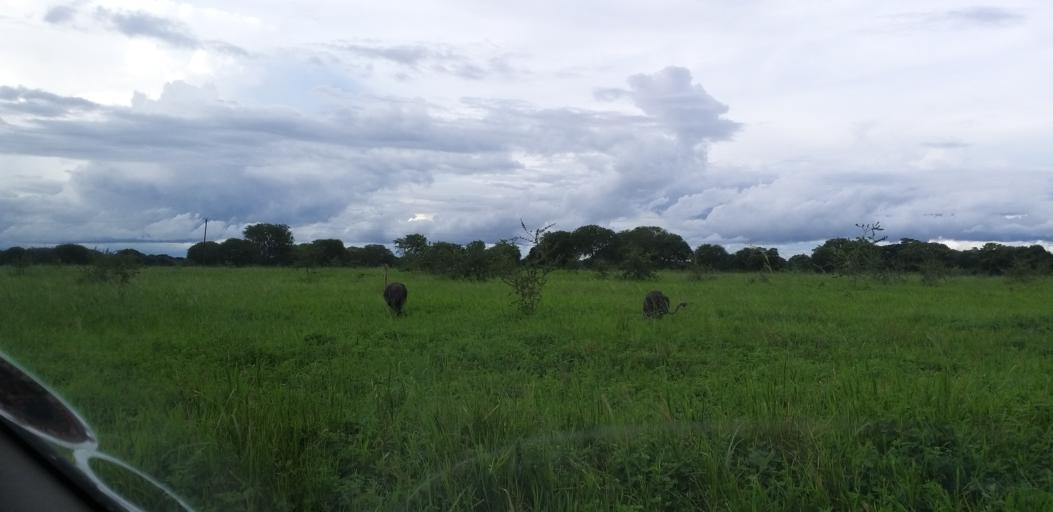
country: ZM
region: Lusaka
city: Chongwe
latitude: -15.1587
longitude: 28.4861
